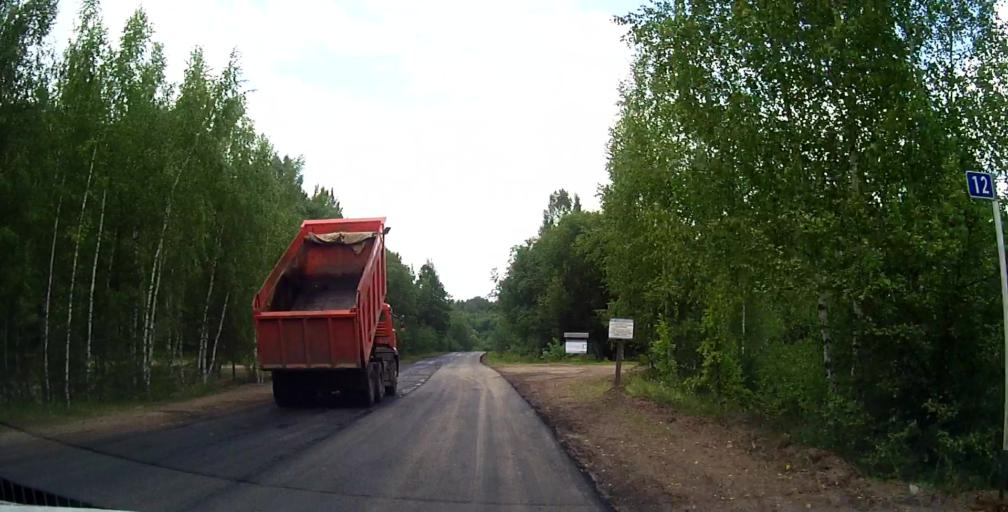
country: RU
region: Smolensk
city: Demidov
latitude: 55.4896
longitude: 31.6370
